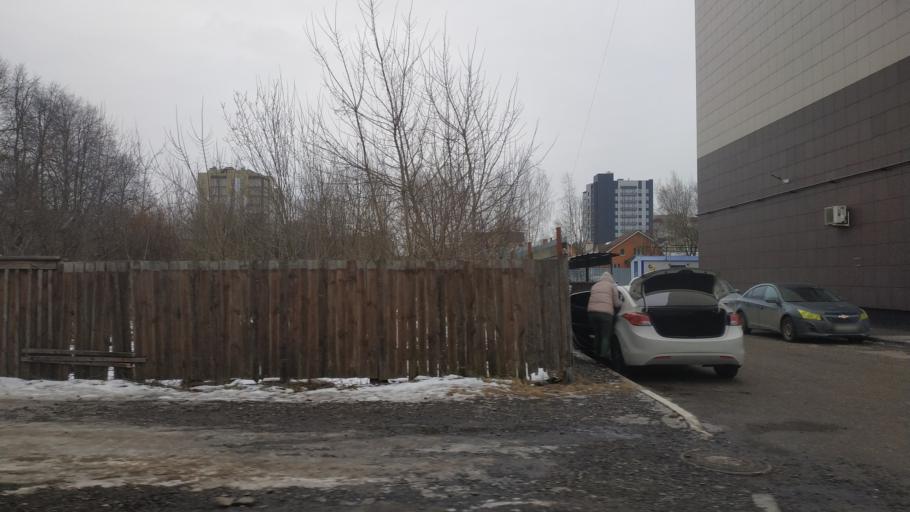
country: RU
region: Tverskaya
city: Tver
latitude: 56.8768
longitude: 35.8920
